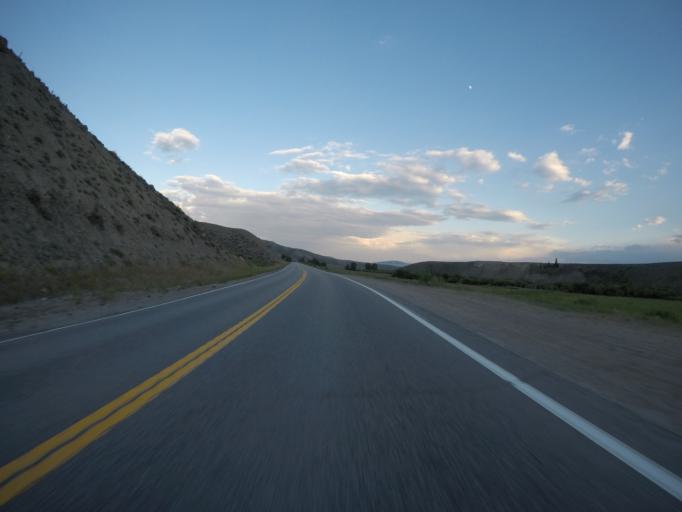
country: US
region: Colorado
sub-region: Grand County
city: Kremmling
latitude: 40.2475
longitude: -106.4499
